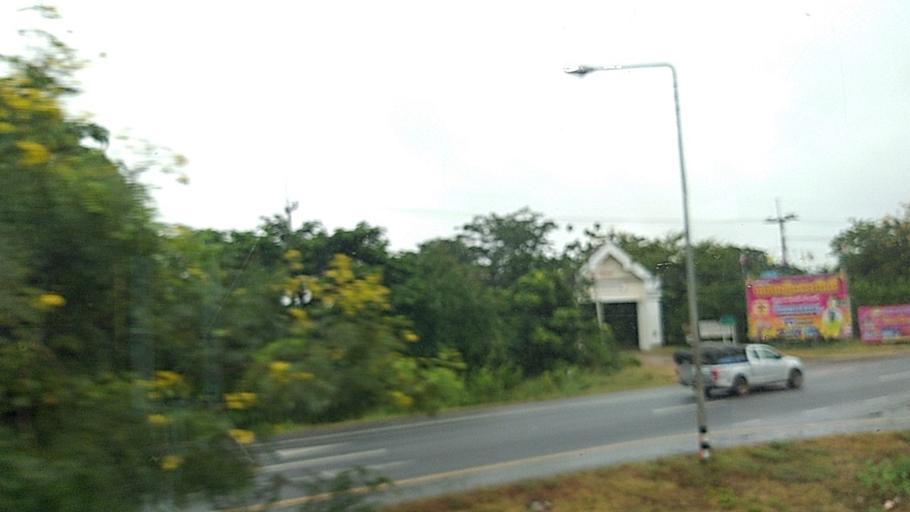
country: TH
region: Nakhon Ratchasima
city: Non Sung
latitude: 15.1451
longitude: 102.3222
